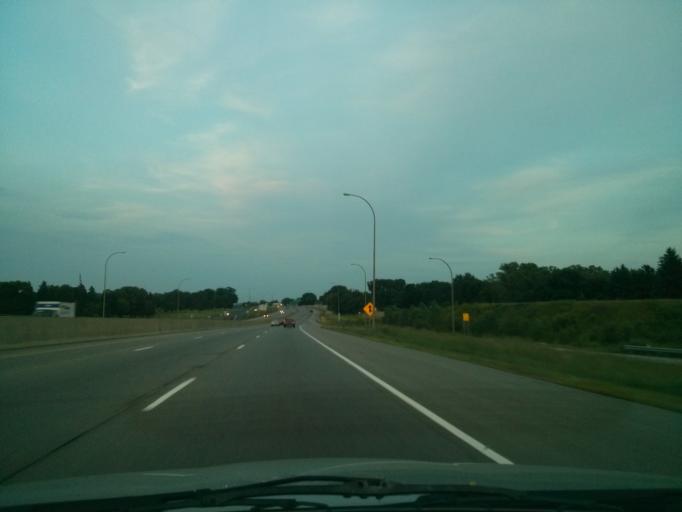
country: US
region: Minnesota
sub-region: Ramsey County
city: Maplewood
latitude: 44.9495
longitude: -92.9994
